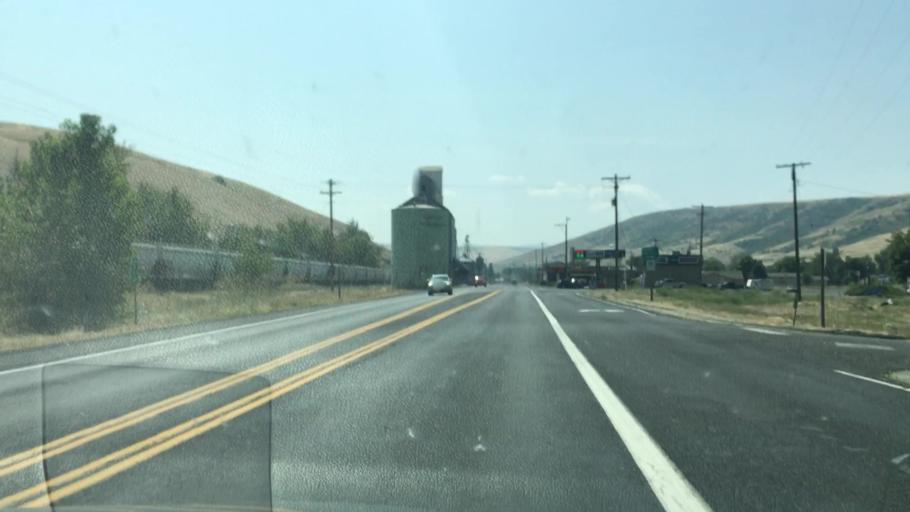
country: US
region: Idaho
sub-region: Nez Perce County
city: Lapwai
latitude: 46.4085
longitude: -116.8021
